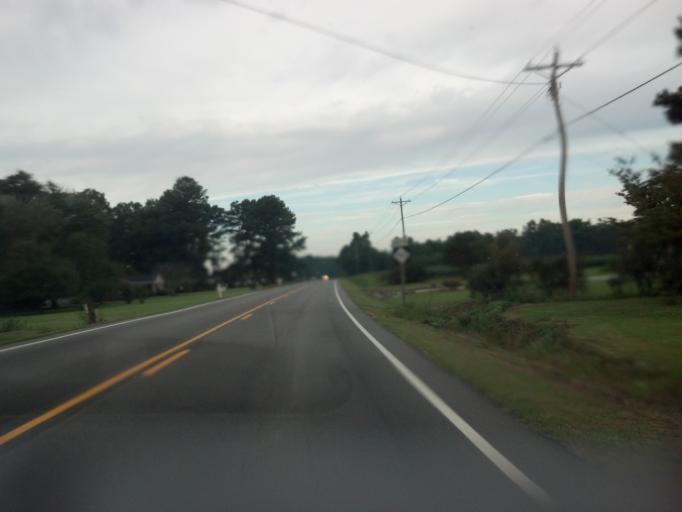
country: US
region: North Carolina
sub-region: Greene County
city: Maury
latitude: 35.4654
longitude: -77.5177
